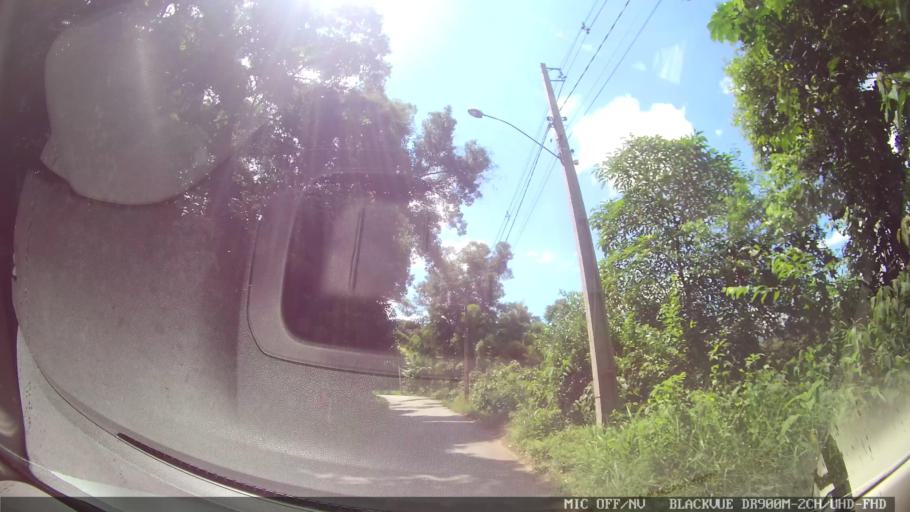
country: BR
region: Minas Gerais
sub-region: Extrema
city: Extrema
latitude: -22.8439
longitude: -46.2911
